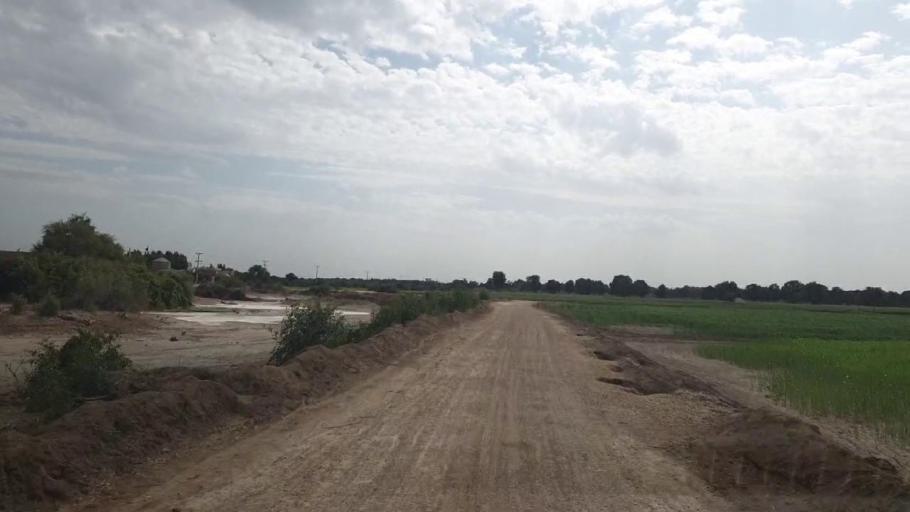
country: PK
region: Sindh
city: Hala
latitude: 25.9231
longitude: 68.4287
